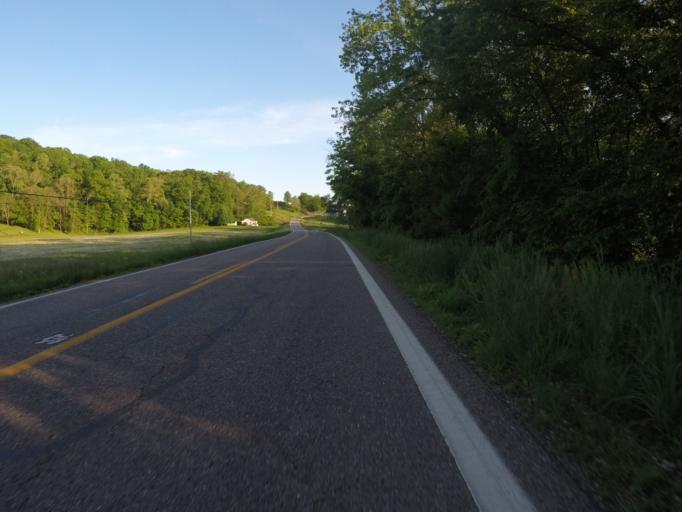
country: US
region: West Virginia
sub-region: Cabell County
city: Huntington
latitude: 38.5356
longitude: -82.4604
